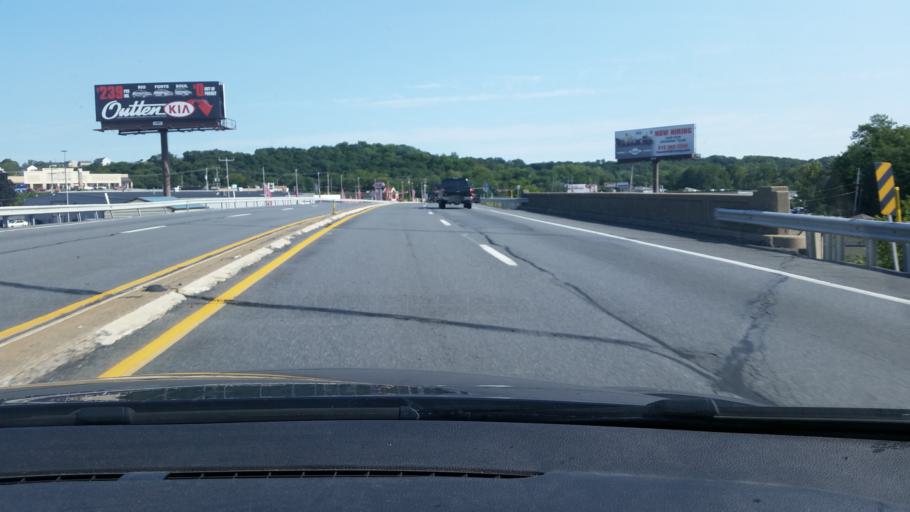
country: US
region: Pennsylvania
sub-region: Berks County
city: Hamburg
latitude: 40.5439
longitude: -75.9806
